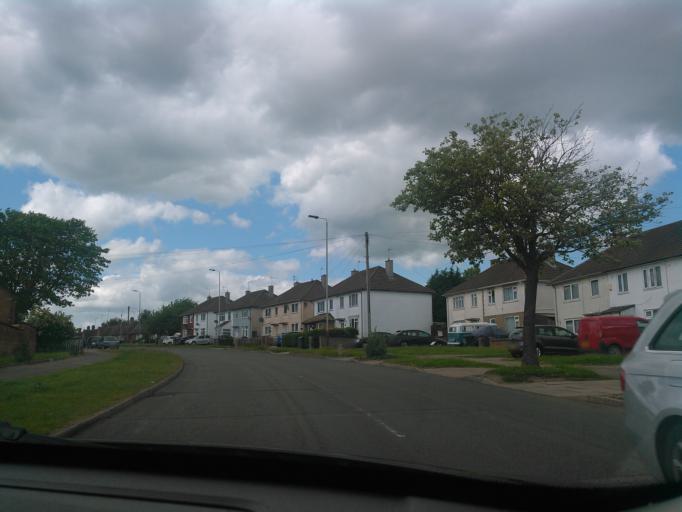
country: GB
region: England
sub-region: Leicestershire
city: Glenfield
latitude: 52.6347
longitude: -1.1911
